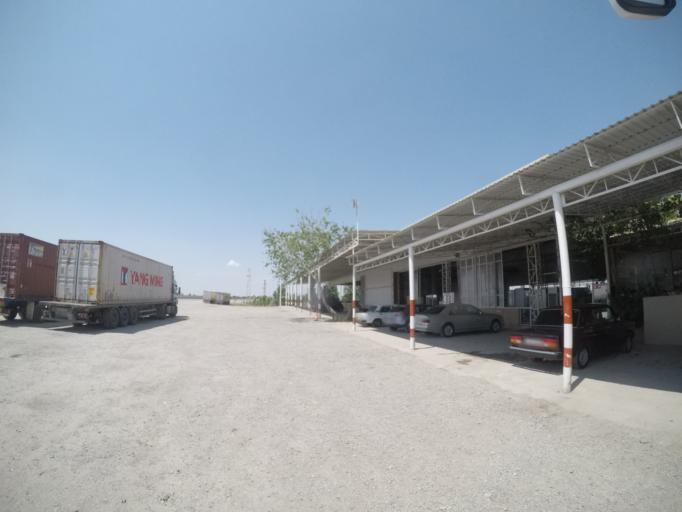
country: AZ
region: Kurdamir Rayon
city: Kyurdarmir
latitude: 40.3158
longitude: 48.1703
